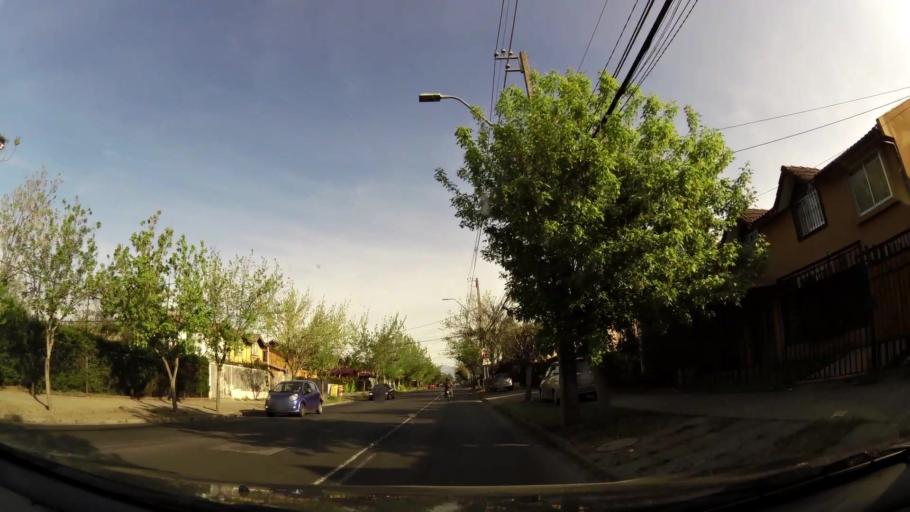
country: CL
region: Santiago Metropolitan
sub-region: Provincia de Cordillera
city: Puente Alto
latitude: -33.5832
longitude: -70.5686
